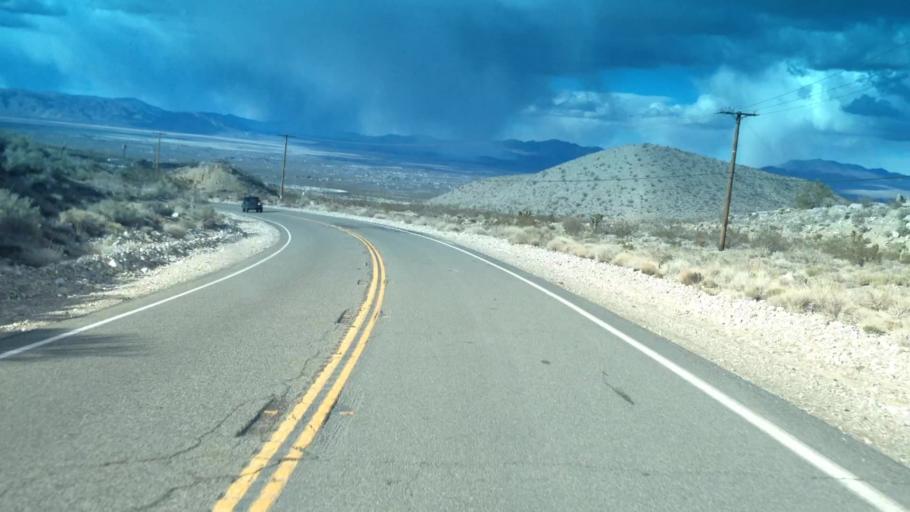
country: US
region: California
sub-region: San Bernardino County
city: Big Bear City
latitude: 34.3614
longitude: -116.8555
